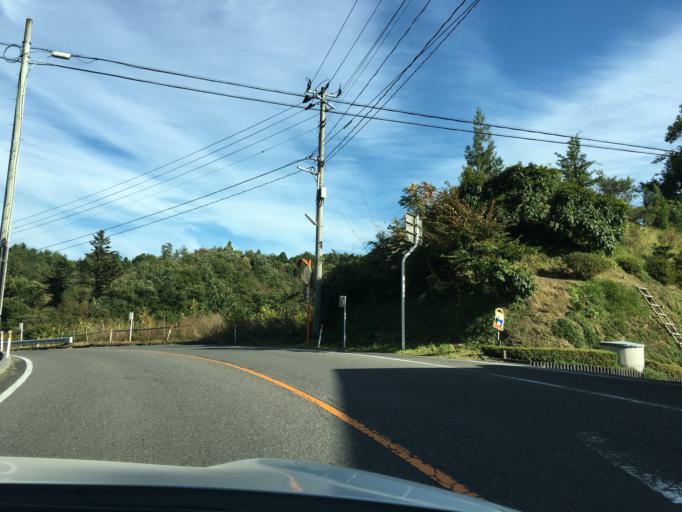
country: JP
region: Fukushima
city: Miharu
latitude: 37.3580
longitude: 140.5150
